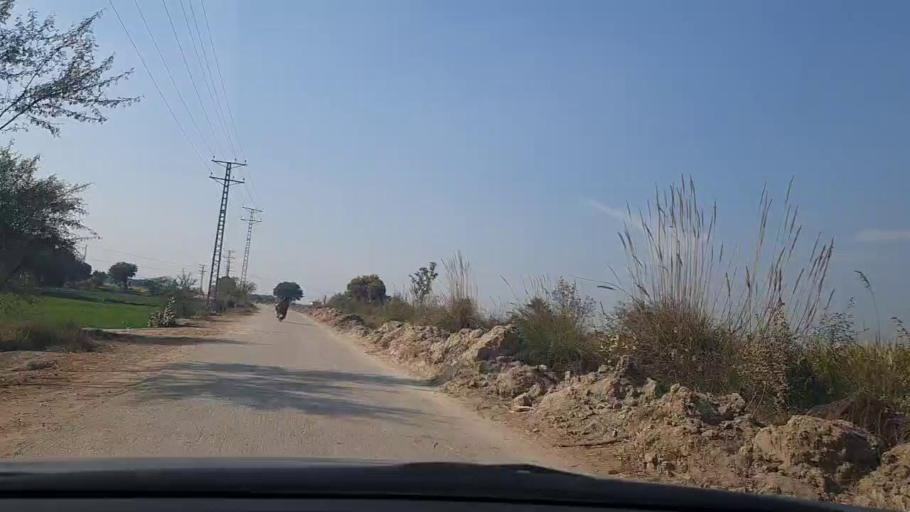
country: PK
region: Sindh
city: Daulatpur
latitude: 26.3084
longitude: 68.0821
